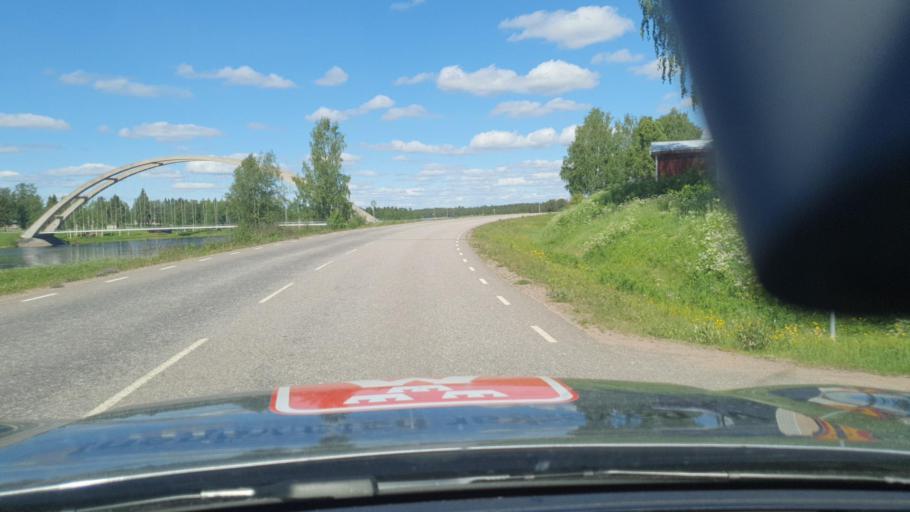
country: SE
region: Norrbotten
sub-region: Pajala Kommun
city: Pajala
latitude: 67.1664
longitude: 22.6159
